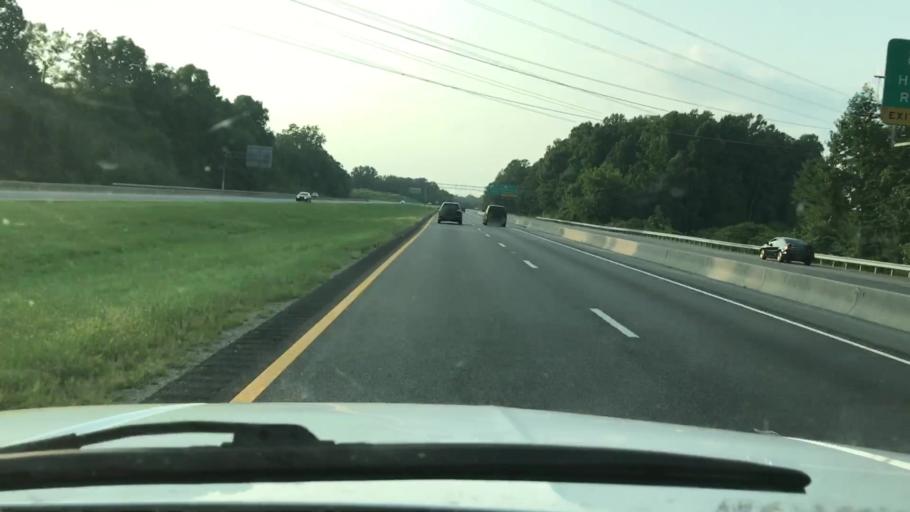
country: US
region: Virginia
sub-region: Chesterfield County
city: Brandermill
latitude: 37.4184
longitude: -77.6249
